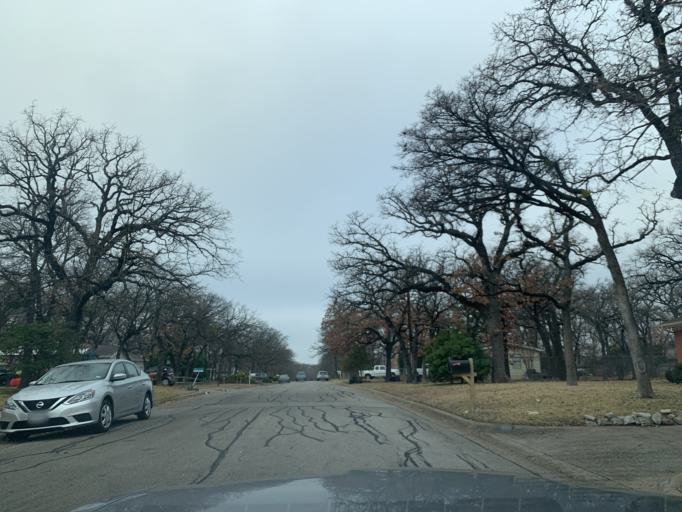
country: US
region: Texas
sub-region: Tarrant County
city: Bedford
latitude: 32.8336
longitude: -97.1474
